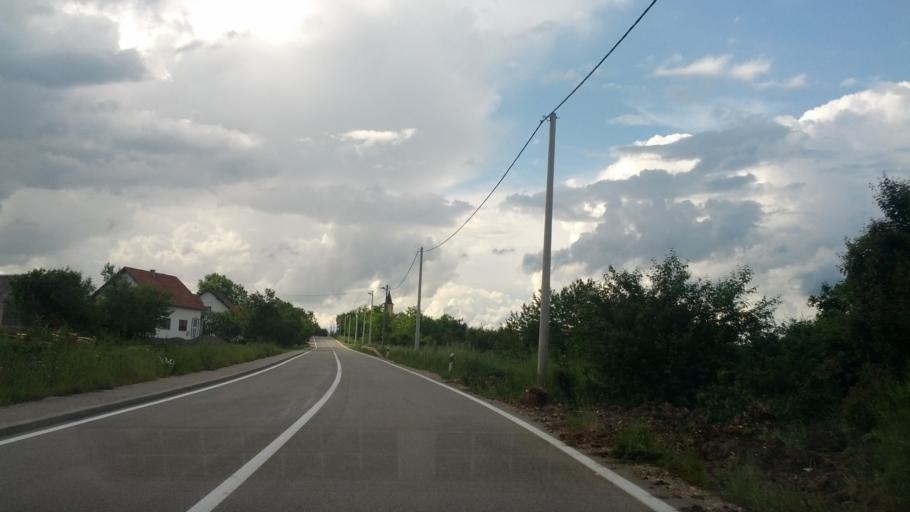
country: BA
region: Federation of Bosnia and Herzegovina
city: Izacic
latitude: 44.9027
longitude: 15.7239
